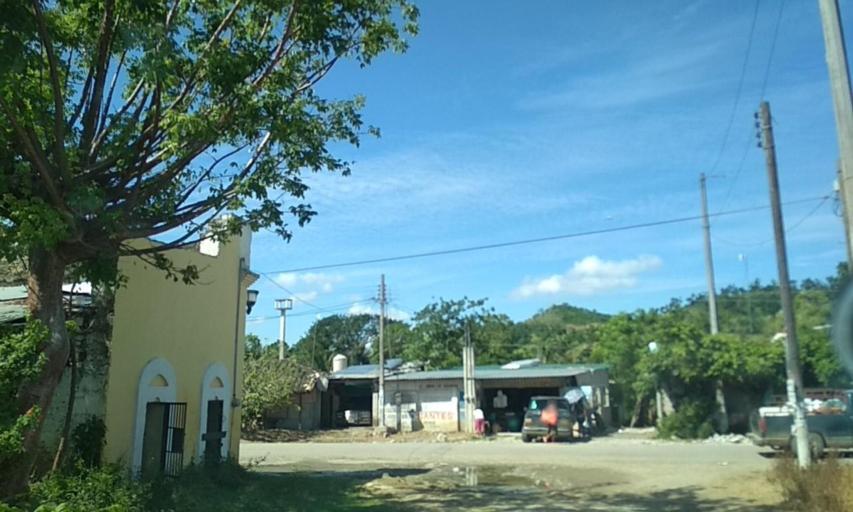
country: MX
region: Veracruz
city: Cazones de Herrera
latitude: 20.6451
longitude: -97.3057
